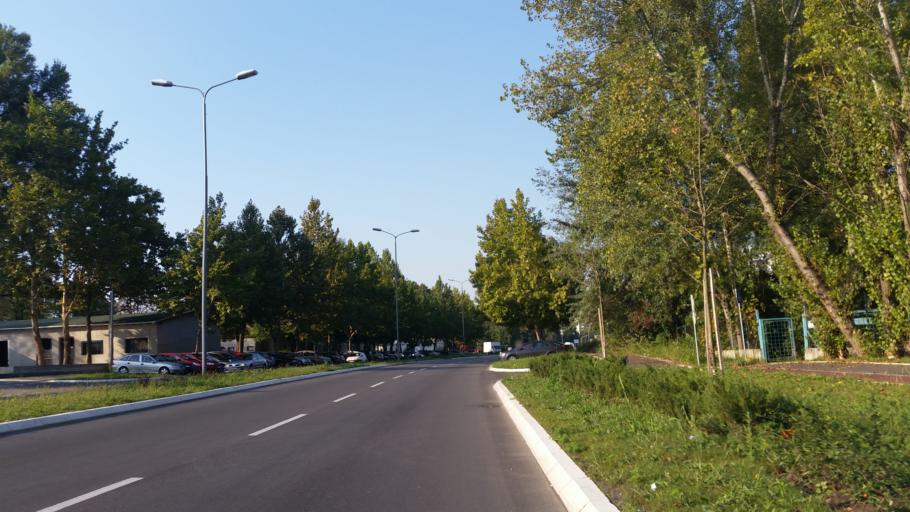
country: RS
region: Central Serbia
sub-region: Belgrade
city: Zemun
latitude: 44.8144
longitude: 20.3933
